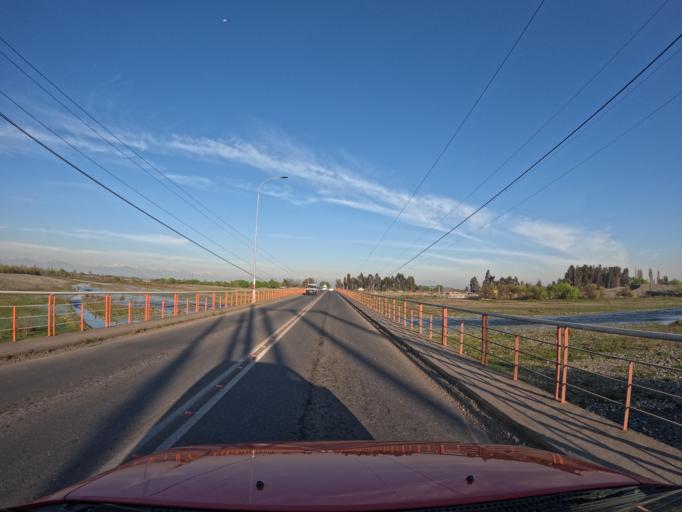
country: CL
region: Maule
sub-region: Provincia de Curico
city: Rauco
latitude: -34.9334
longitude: -71.2755
